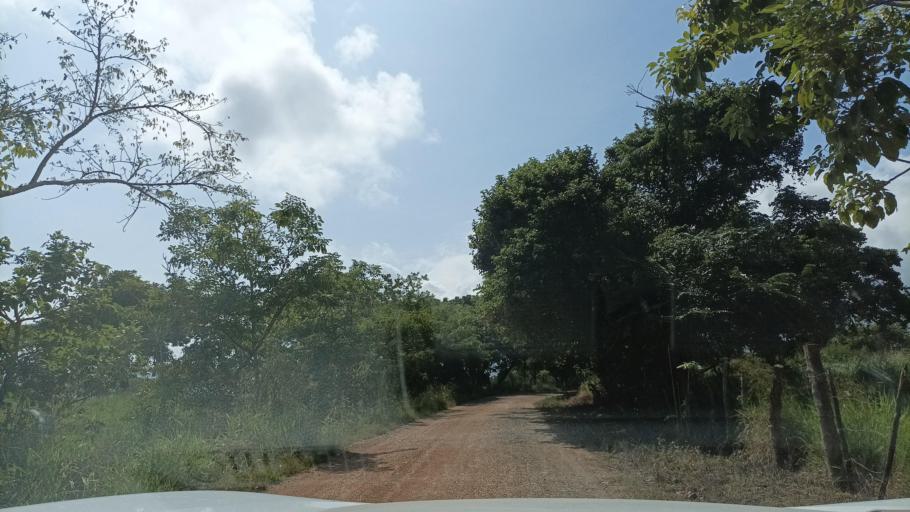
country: MX
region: Veracruz
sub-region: Chinameca
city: Chacalapa
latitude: 18.1208
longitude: -94.6554
